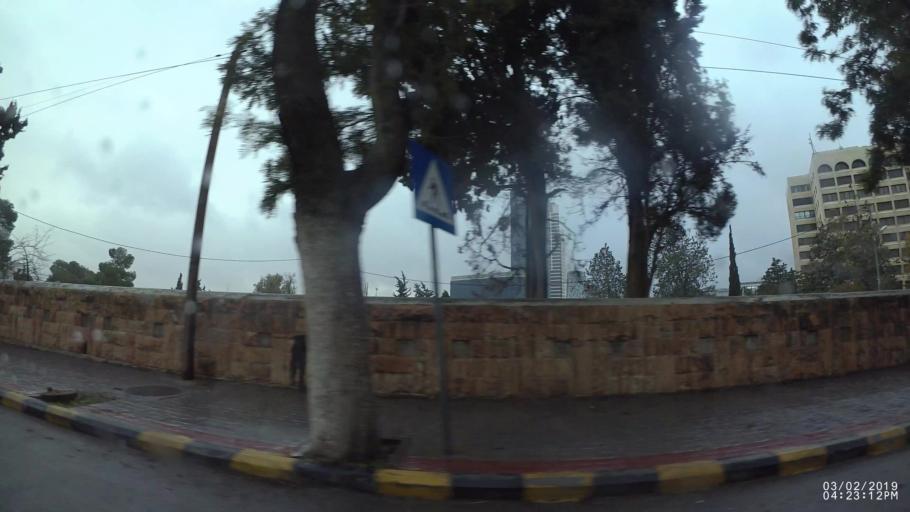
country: JO
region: Amman
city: Amman
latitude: 31.9667
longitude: 35.9116
